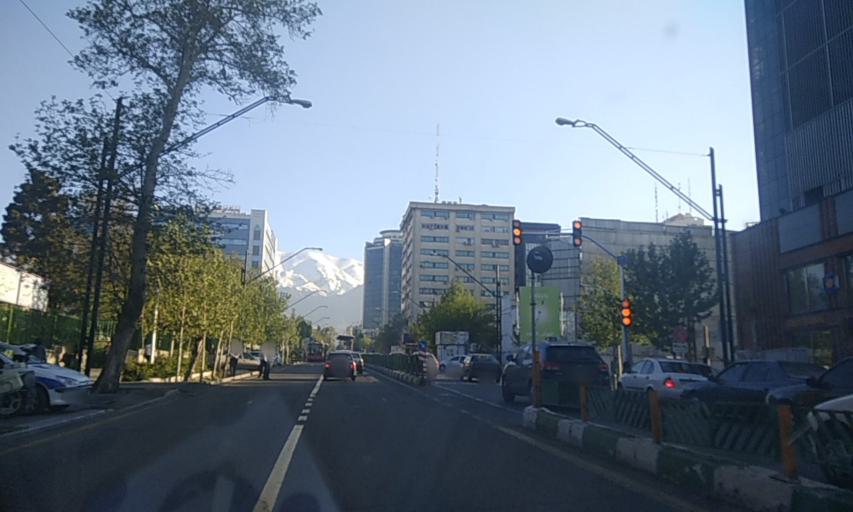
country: IR
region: Tehran
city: Tajrish
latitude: 35.7661
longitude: 51.4108
